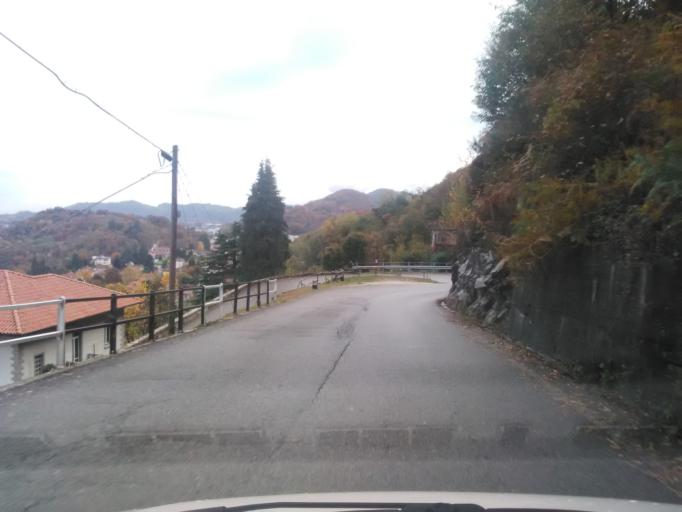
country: IT
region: Piedmont
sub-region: Provincia Verbano-Cusio-Ossola
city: Madonna del Sasso
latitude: 45.7946
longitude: 8.3764
